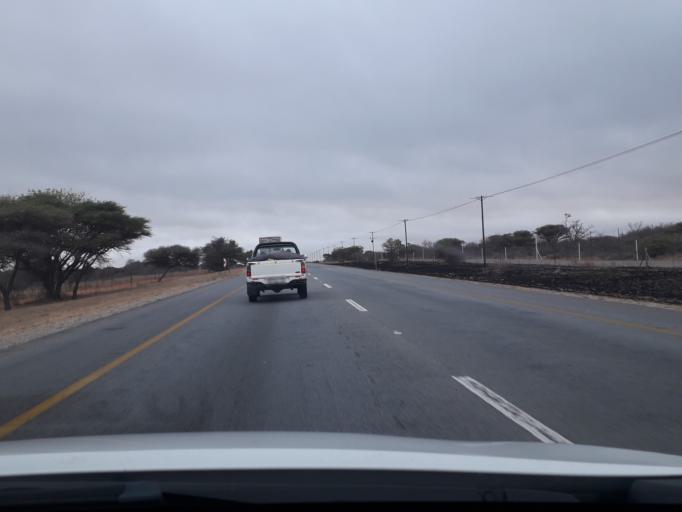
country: ZA
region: Limpopo
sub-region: Capricorn District Municipality
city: Mankoeng
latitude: -23.5884
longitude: 29.6637
